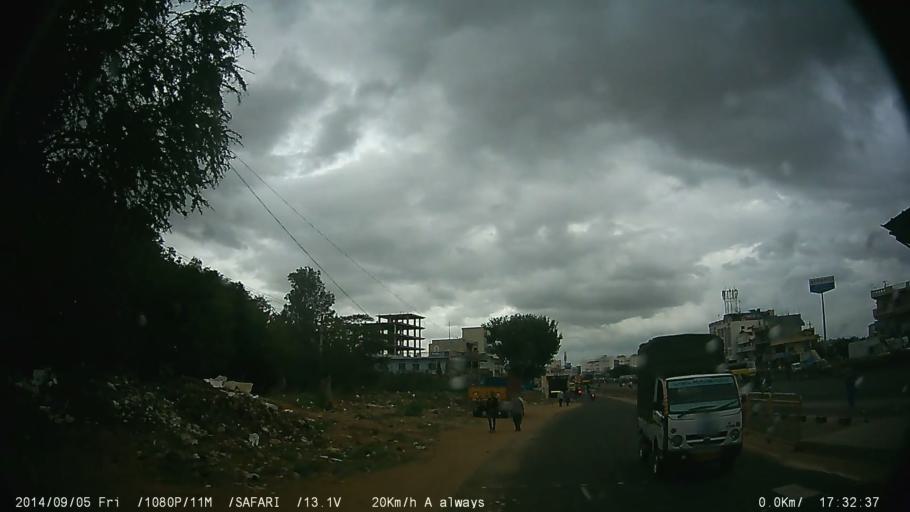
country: IN
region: Karnataka
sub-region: Bangalore Urban
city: Anekal
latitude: 12.8064
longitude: 77.6993
